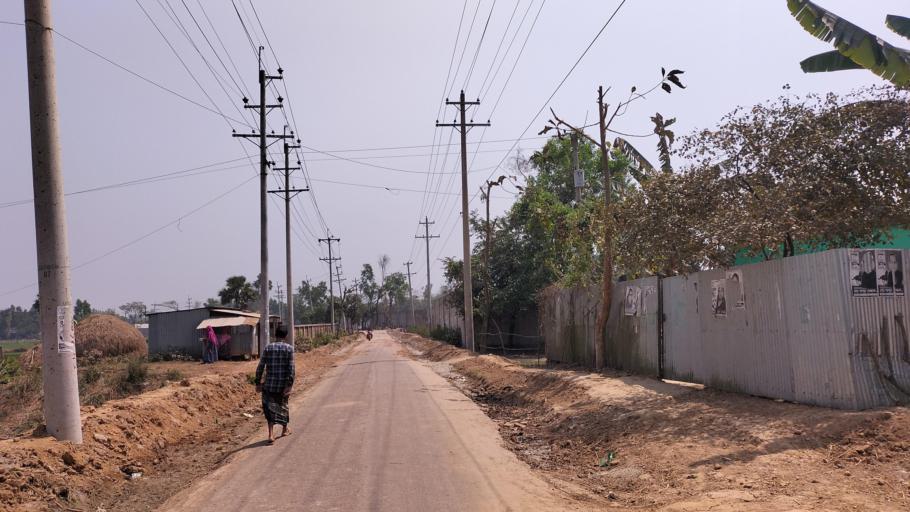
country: BD
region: Dhaka
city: Sakhipur
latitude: 24.3089
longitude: 90.2936
